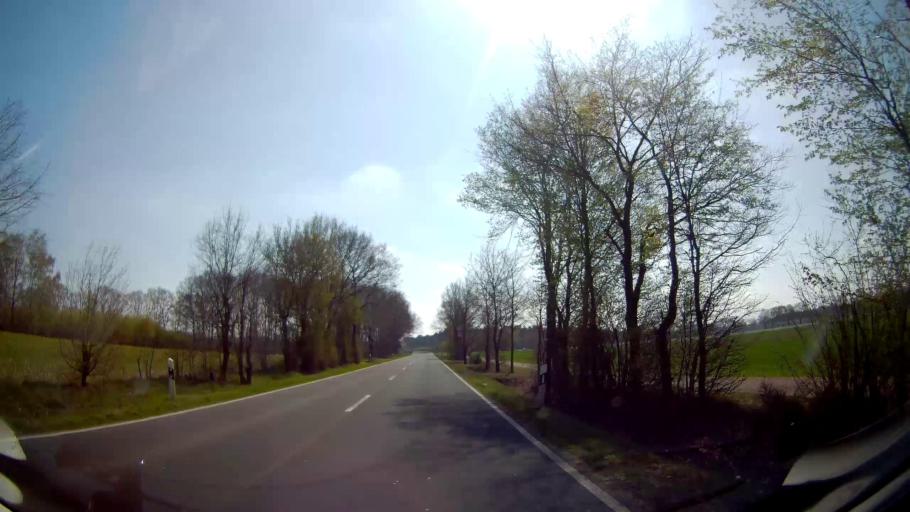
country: DE
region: North Rhine-Westphalia
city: Dorsten
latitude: 51.6973
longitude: 7.0093
